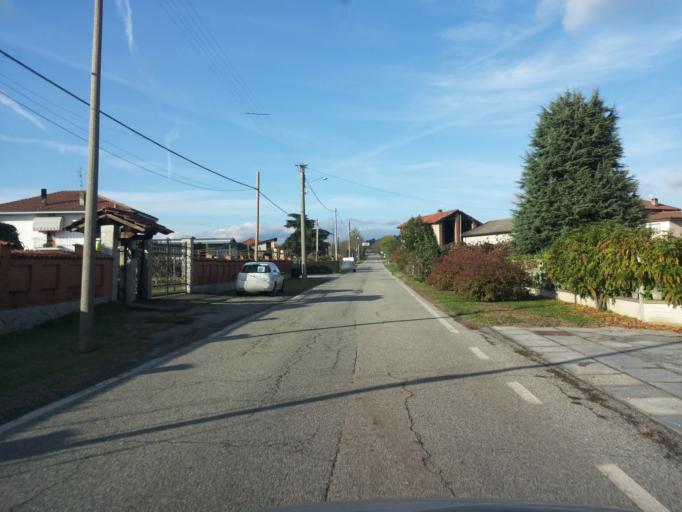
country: IT
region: Piedmont
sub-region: Provincia di Vercelli
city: Alice Castello
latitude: 45.3750
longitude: 8.0728
